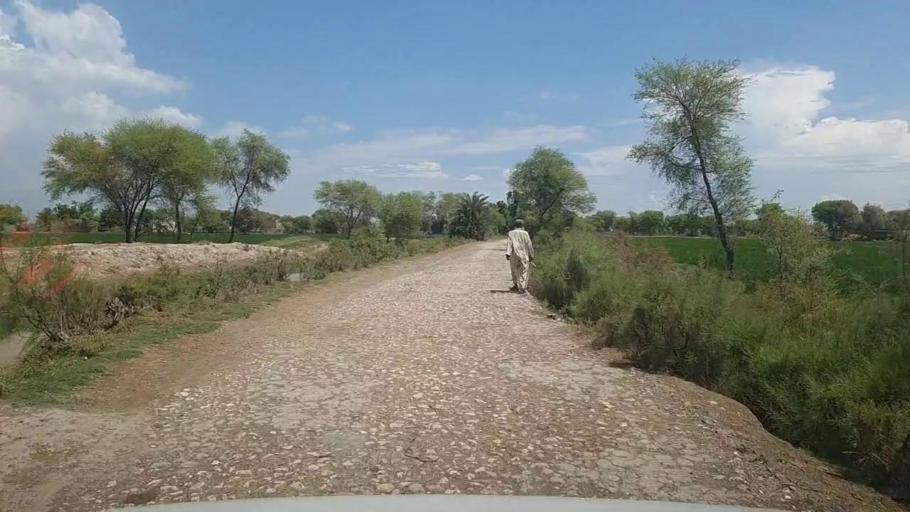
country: PK
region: Sindh
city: Kandhkot
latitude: 28.3411
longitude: 69.2405
